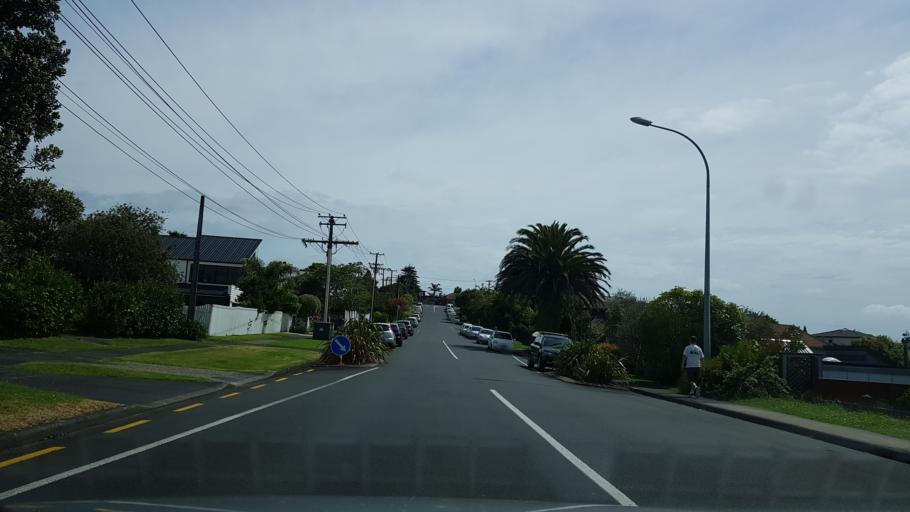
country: NZ
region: Auckland
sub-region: Auckland
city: North Shore
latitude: -36.8128
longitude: 174.7093
